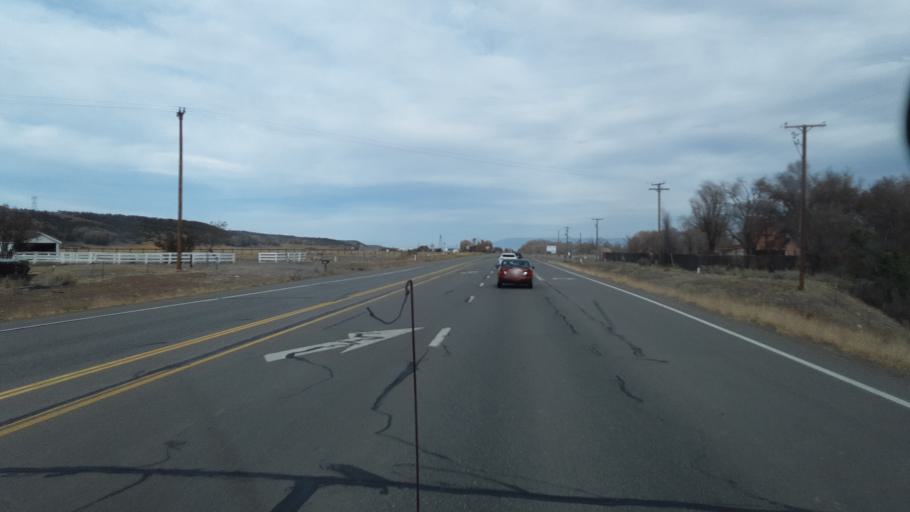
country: US
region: Colorado
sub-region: Montrose County
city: Montrose
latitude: 38.3276
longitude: -107.7800
